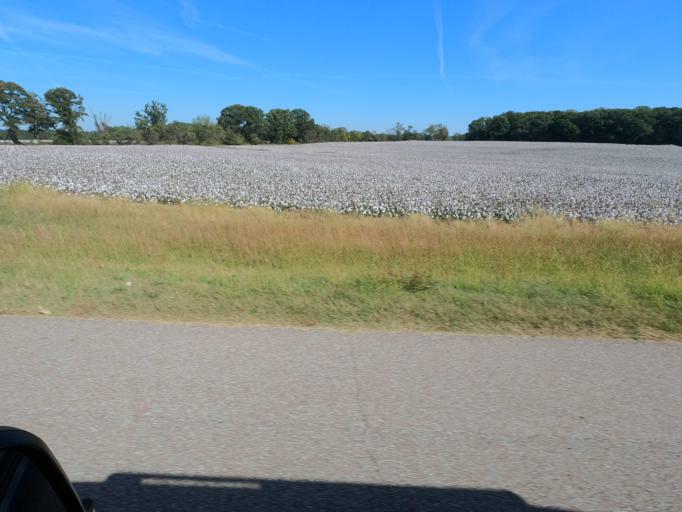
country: US
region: Tennessee
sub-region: Crockett County
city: Alamo
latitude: 35.8705
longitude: -89.2151
